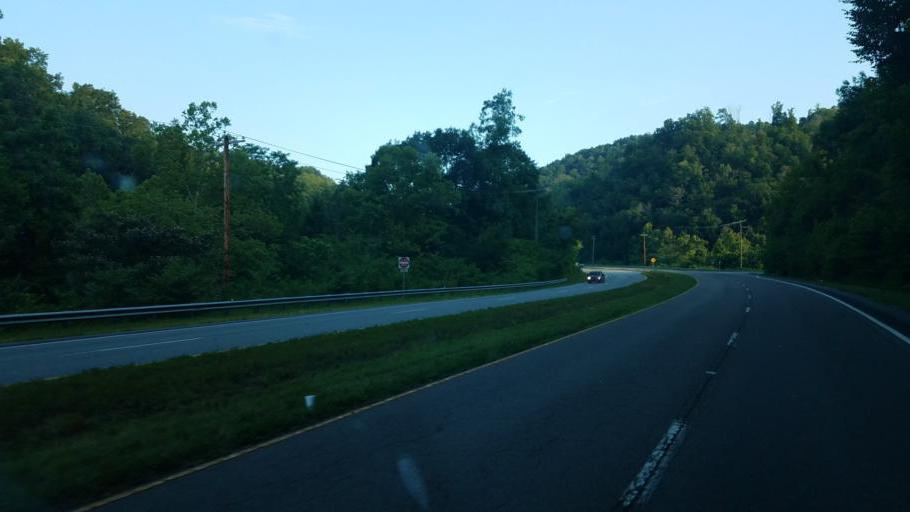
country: US
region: Tennessee
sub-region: Hawkins County
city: Church Hill
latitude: 36.6762
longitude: -82.7560
